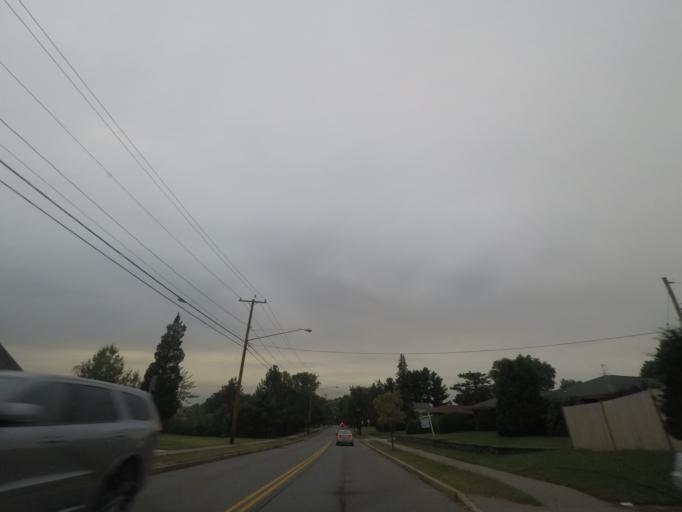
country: US
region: New York
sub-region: Albany County
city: Delmar
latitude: 42.6533
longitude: -73.8150
